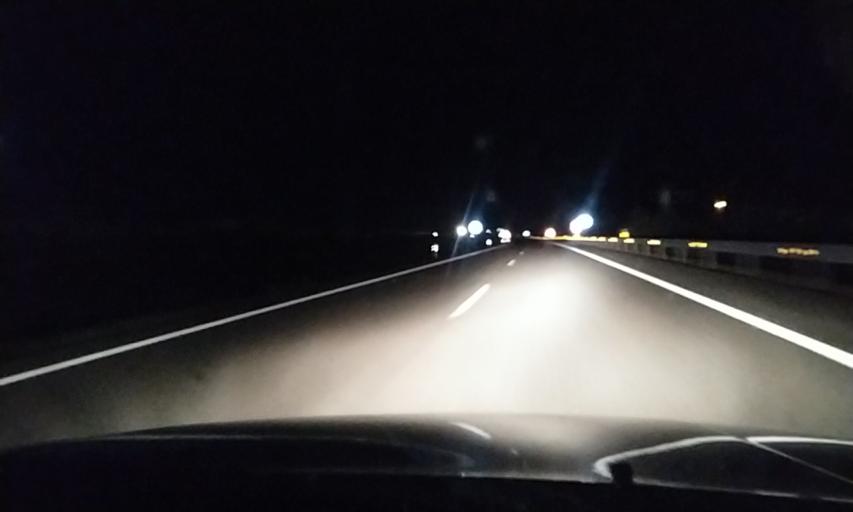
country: ES
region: Castille and Leon
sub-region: Provincia de Leon
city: La Baneza
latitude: 42.2867
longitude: -5.9150
